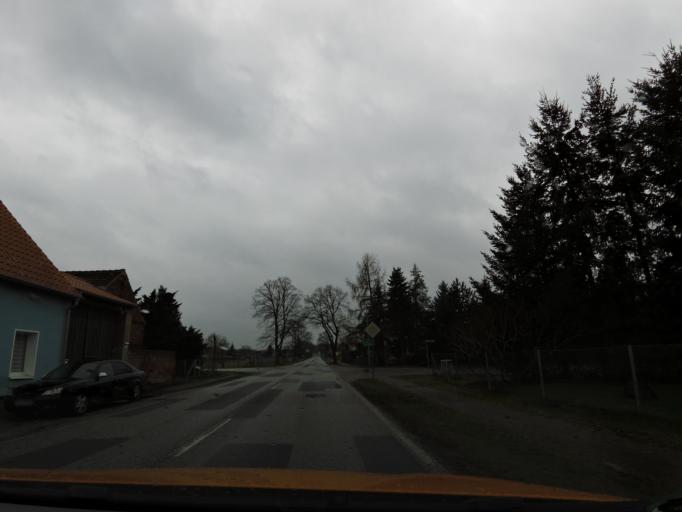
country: DE
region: Brandenburg
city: Ziesar
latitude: 52.2853
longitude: 12.3306
